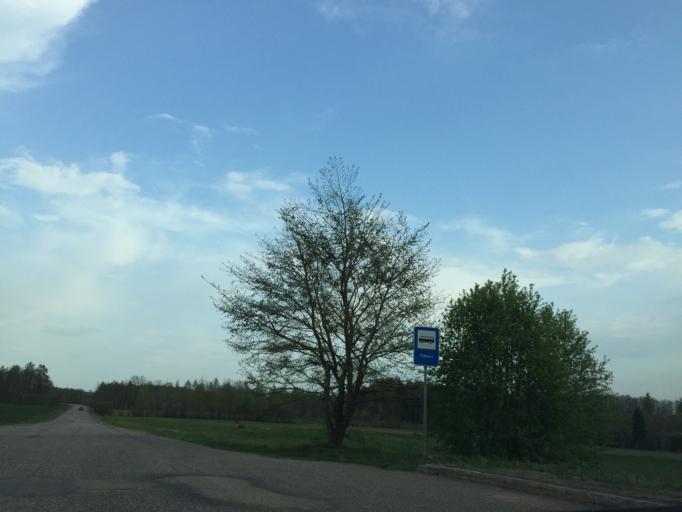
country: LV
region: Malpils
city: Malpils
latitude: 57.0133
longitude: 24.8918
